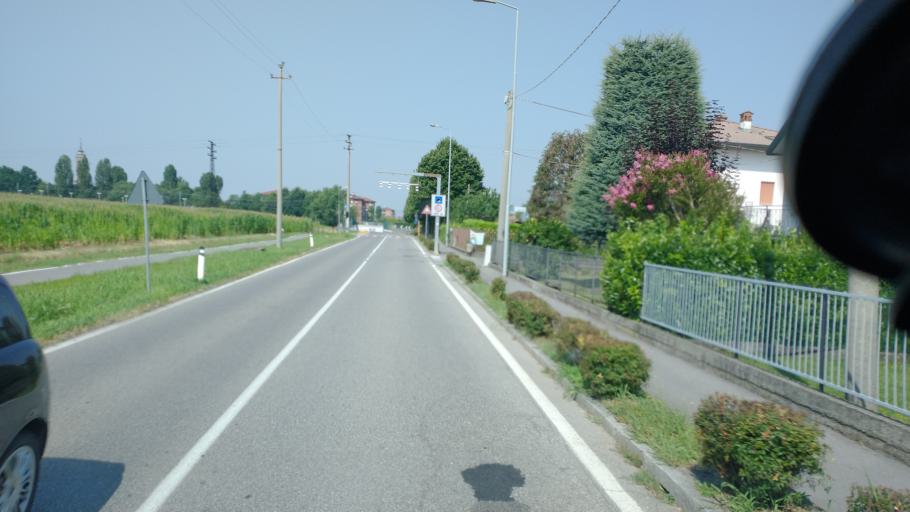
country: IT
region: Lombardy
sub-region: Provincia di Bergamo
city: Levate
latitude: 45.6268
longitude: 9.6328
